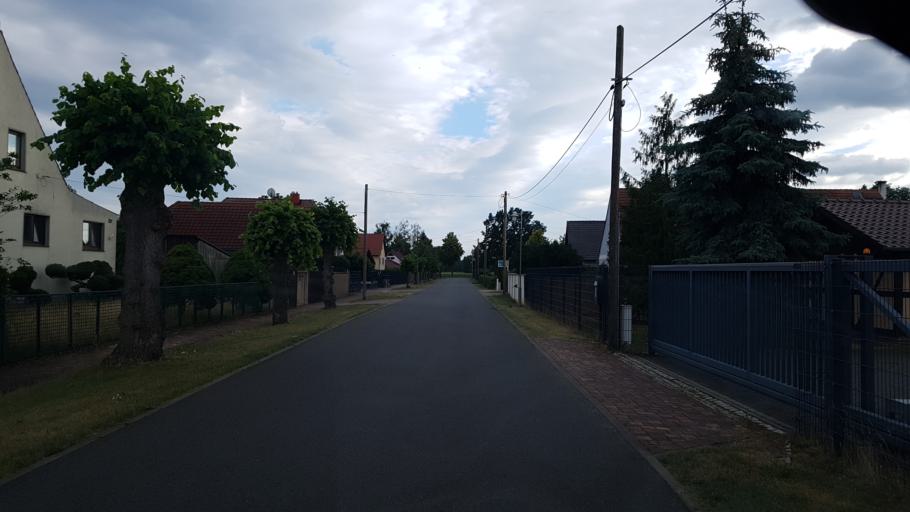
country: DE
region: Brandenburg
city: Kasel-Golzig
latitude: 51.9889
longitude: 13.6904
